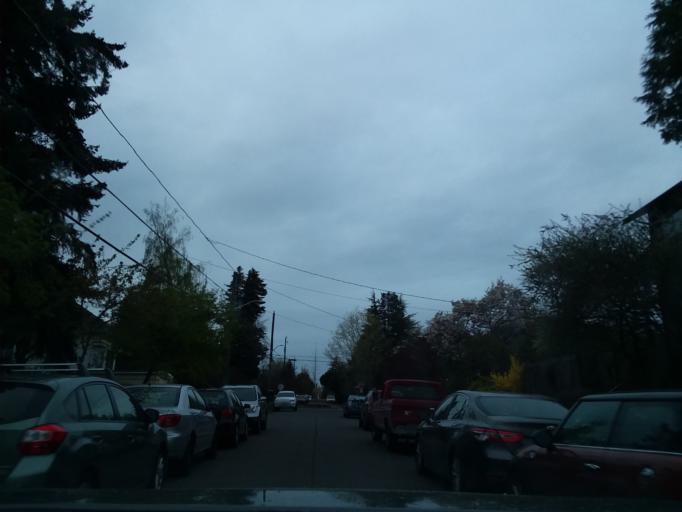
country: US
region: Washington
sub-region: King County
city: Seattle
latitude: 47.6703
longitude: -122.3957
